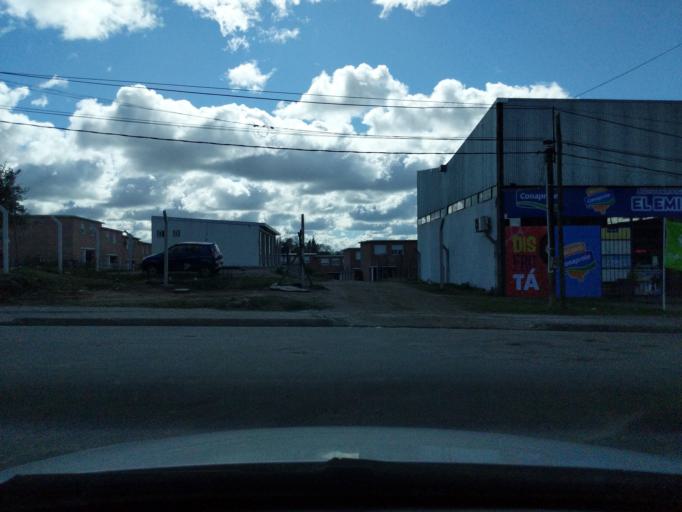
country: UY
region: Florida
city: Florida
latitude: -34.0908
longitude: -56.2276
